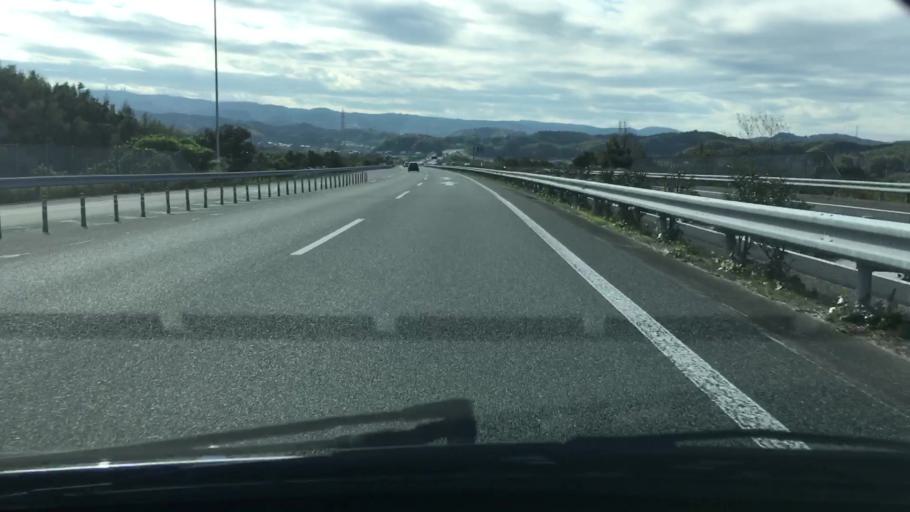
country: JP
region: Chiba
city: Kimitsu
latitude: 35.3191
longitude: 139.9439
